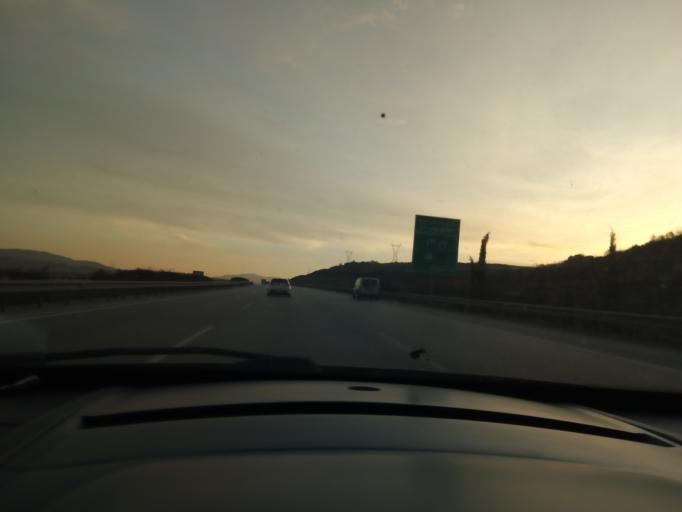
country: TR
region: Bursa
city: Niluefer
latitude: 40.2752
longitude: 28.9762
